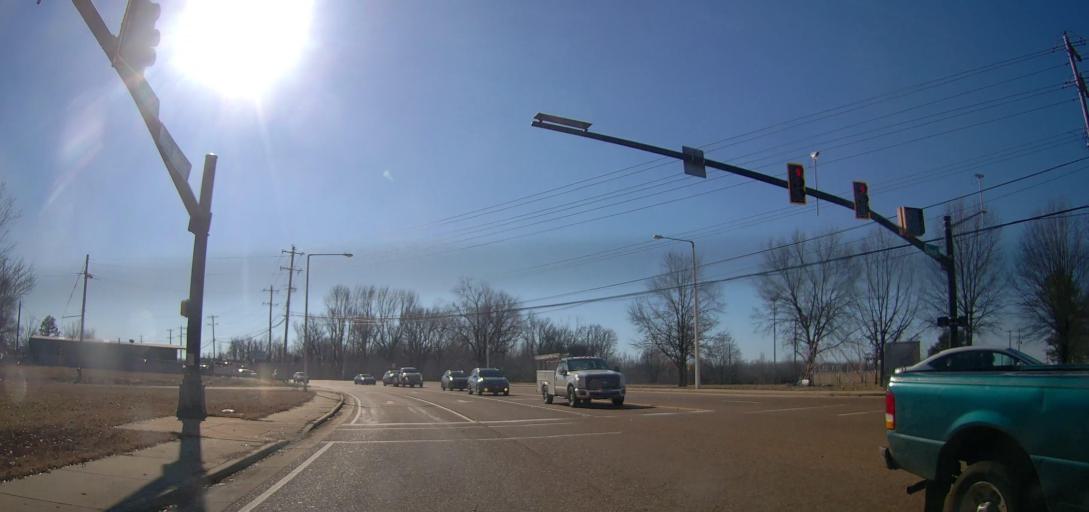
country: US
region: Tennessee
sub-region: Shelby County
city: Millington
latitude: 35.3354
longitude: -89.8976
